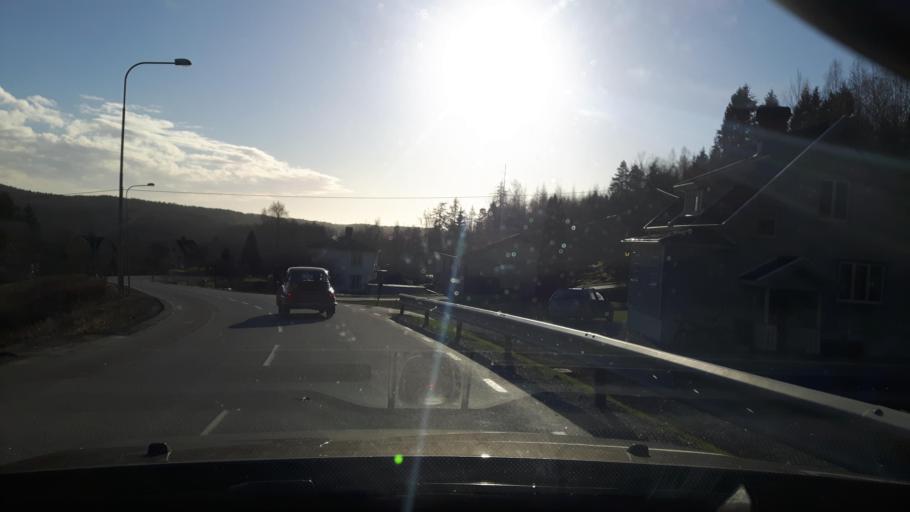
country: SE
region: Vaestra Goetaland
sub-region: Munkedals Kommun
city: Munkedal
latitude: 58.4925
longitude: 11.6947
